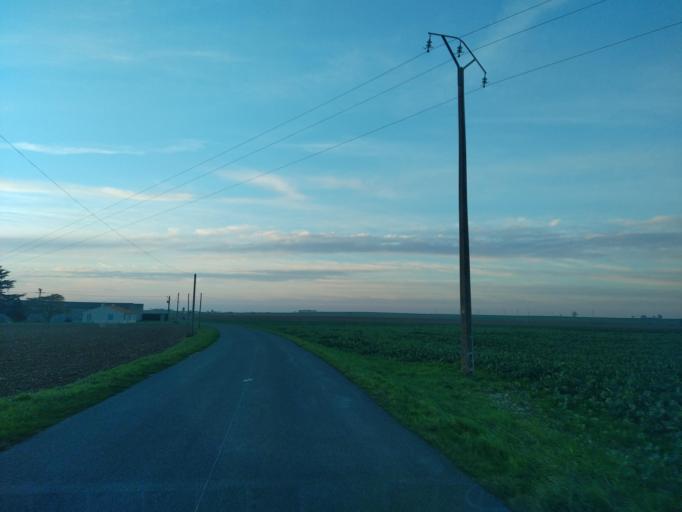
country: FR
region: Pays de la Loire
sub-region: Departement de la Vendee
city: Vix
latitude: 46.4006
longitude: -0.8492
